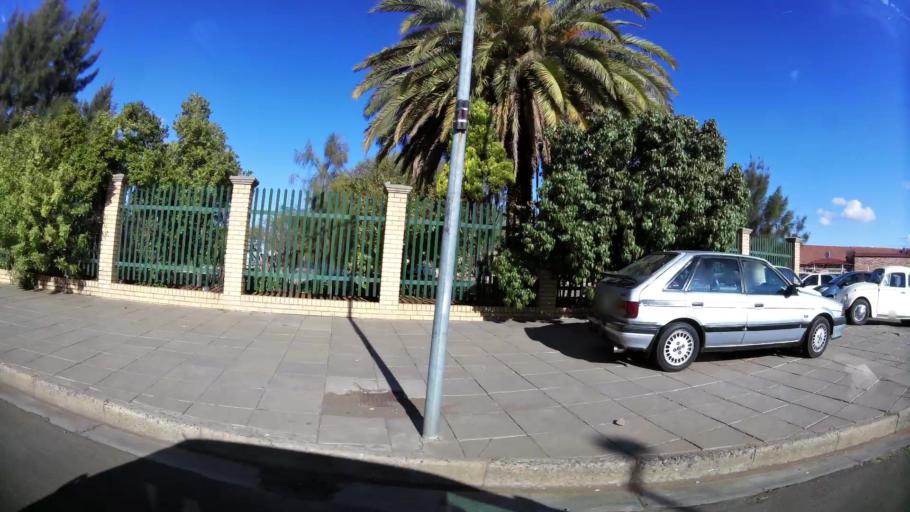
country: ZA
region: Northern Cape
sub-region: Frances Baard District Municipality
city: Kimberley
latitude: -28.7465
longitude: 24.7644
